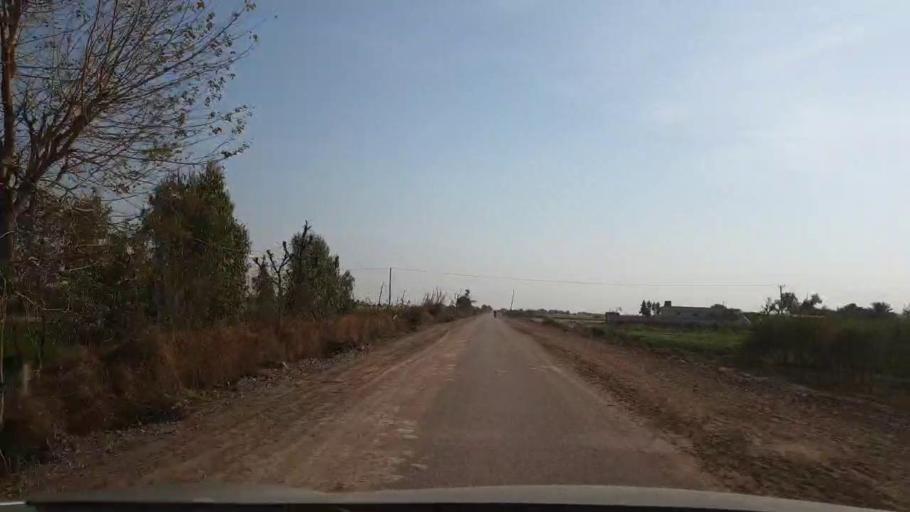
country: PK
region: Sindh
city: Berani
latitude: 25.7291
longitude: 68.8066
